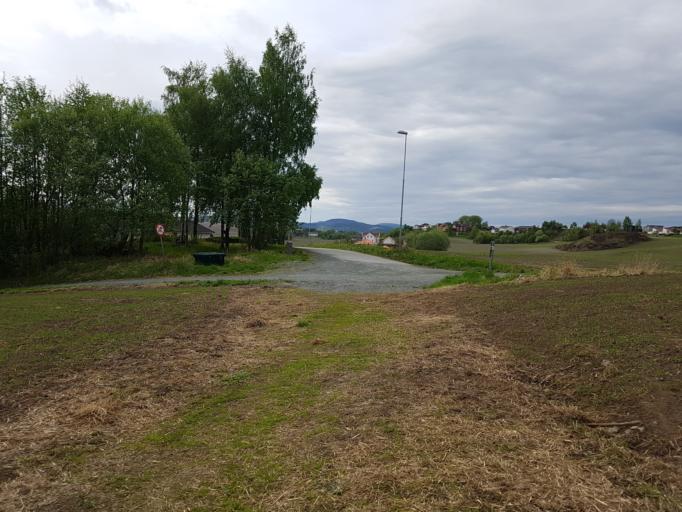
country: NO
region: Nord-Trondelag
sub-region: Levanger
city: Levanger
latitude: 63.7388
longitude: 11.2579
